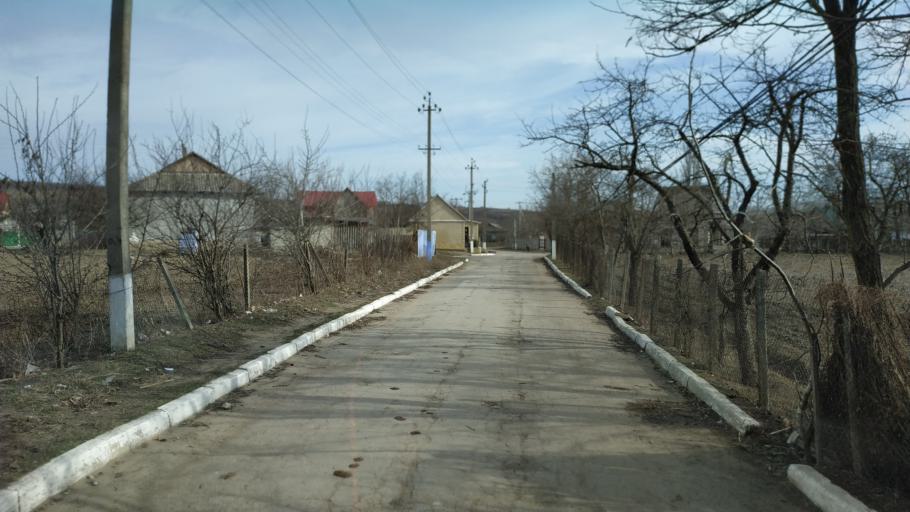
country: RO
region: Vaslui
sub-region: Comuna Dranceni
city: Dranceni
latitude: 46.8787
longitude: 28.1614
